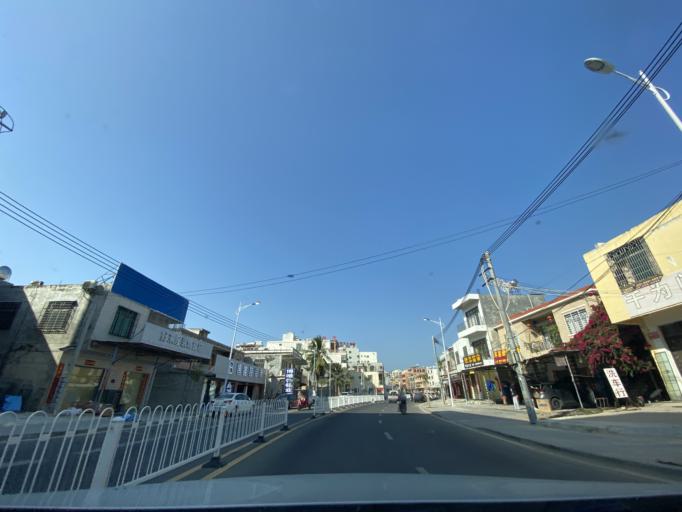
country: CN
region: Hainan
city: Yingzhou
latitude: 18.4198
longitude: 109.8541
